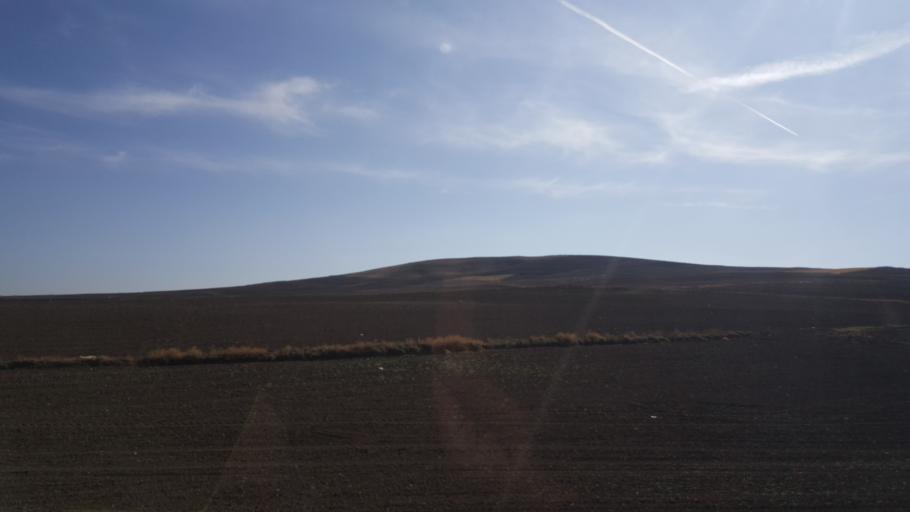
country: TR
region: Ankara
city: Yenice
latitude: 39.3723
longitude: 32.7231
